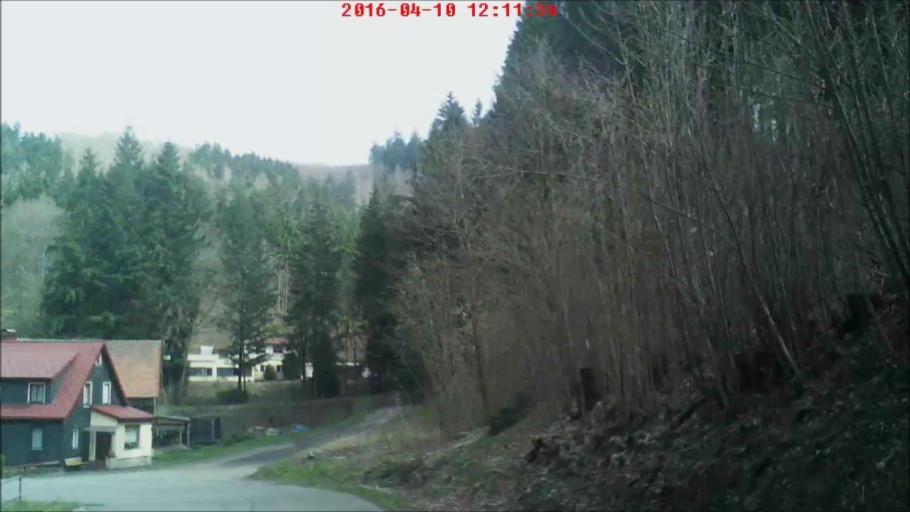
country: DE
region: Thuringia
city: Benshausen
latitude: 50.6690
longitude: 10.6022
